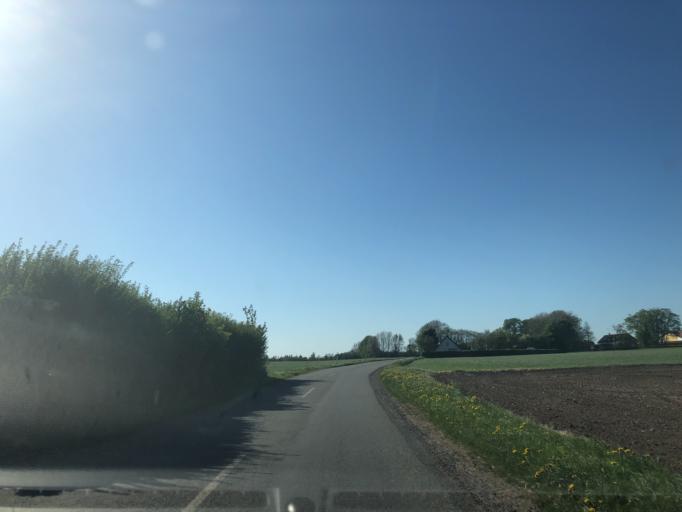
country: DK
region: Zealand
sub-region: Ringsted Kommune
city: Ringsted
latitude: 55.4674
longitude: 11.6987
